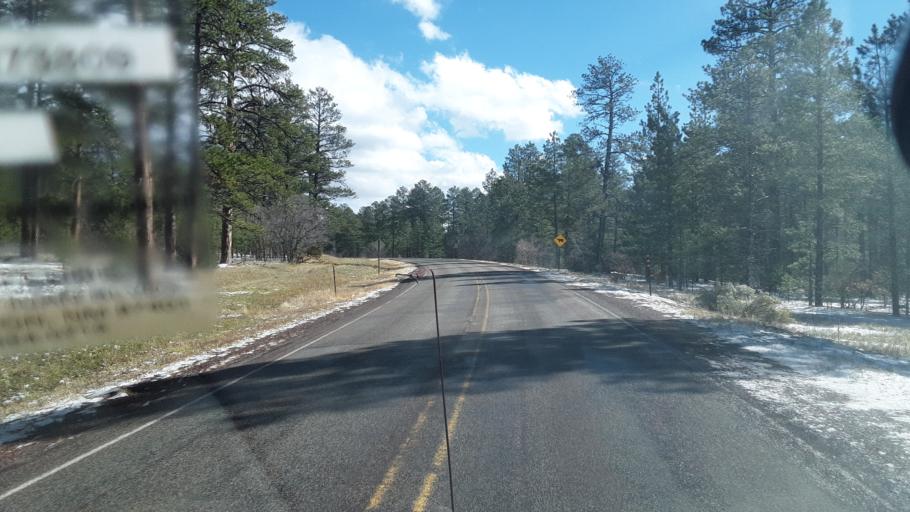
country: US
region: New Mexico
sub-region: Rio Arriba County
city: Santa Teresa
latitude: 36.2000
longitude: -106.7698
